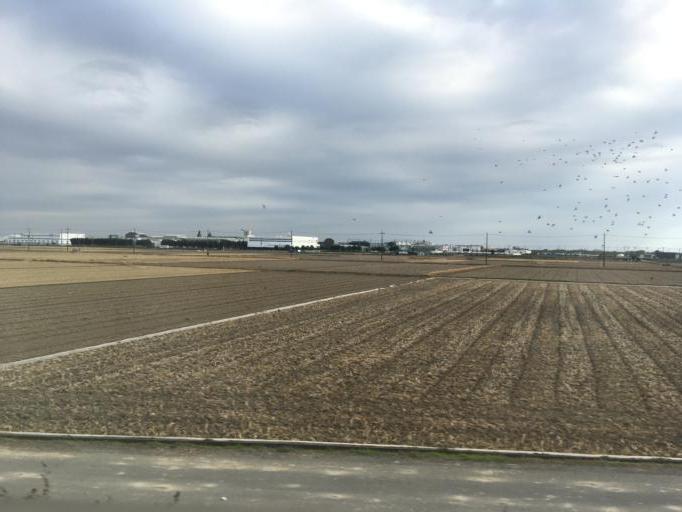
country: JP
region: Tochigi
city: Ashikaga
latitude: 36.3138
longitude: 139.5092
